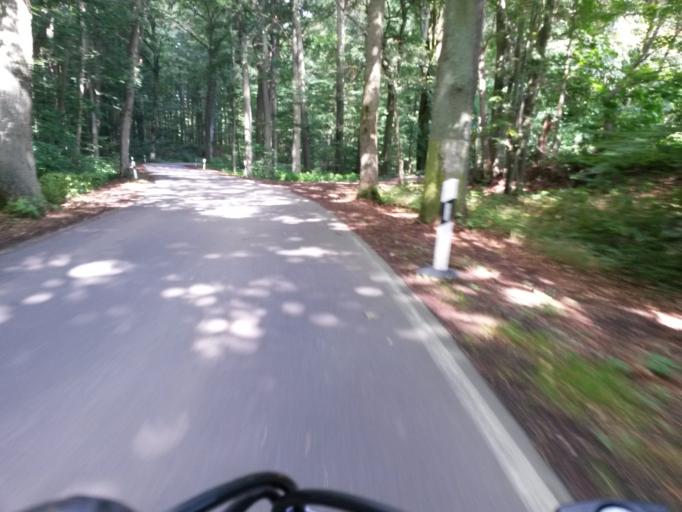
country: DE
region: Brandenburg
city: Angermunde
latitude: 53.0091
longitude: 13.9364
